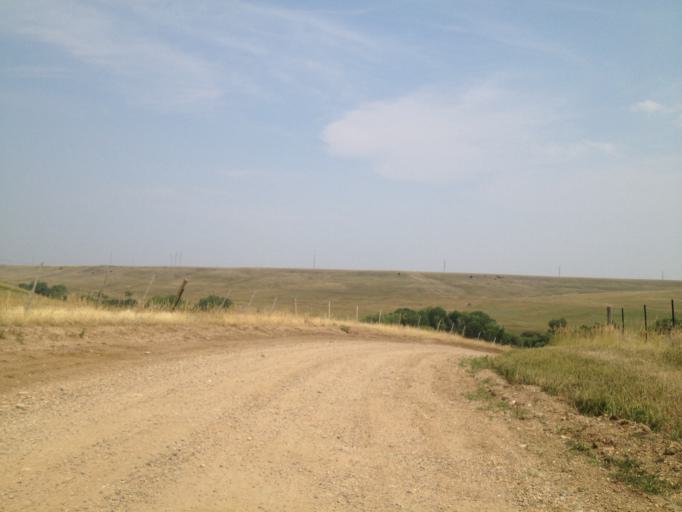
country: US
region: Colorado
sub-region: Boulder County
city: Superior
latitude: 39.9399
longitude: -105.1983
